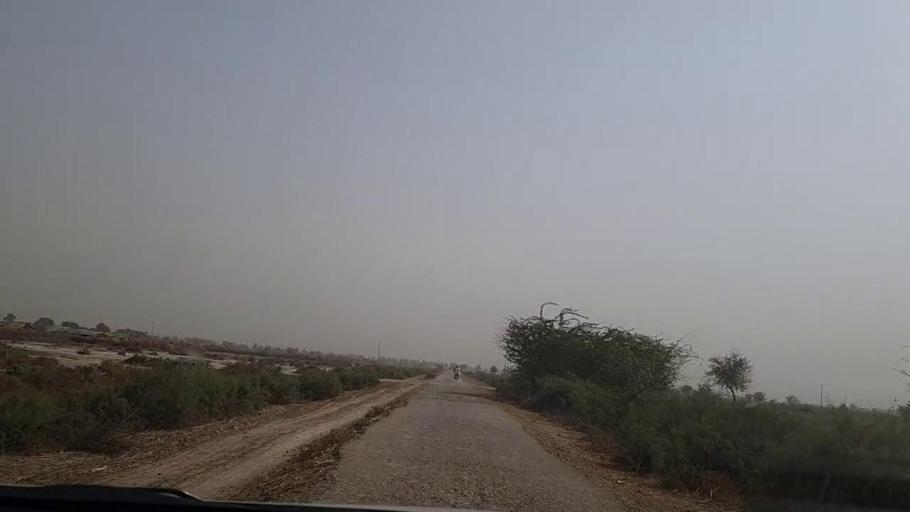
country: PK
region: Sindh
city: Pithoro
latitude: 25.4754
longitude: 69.2259
